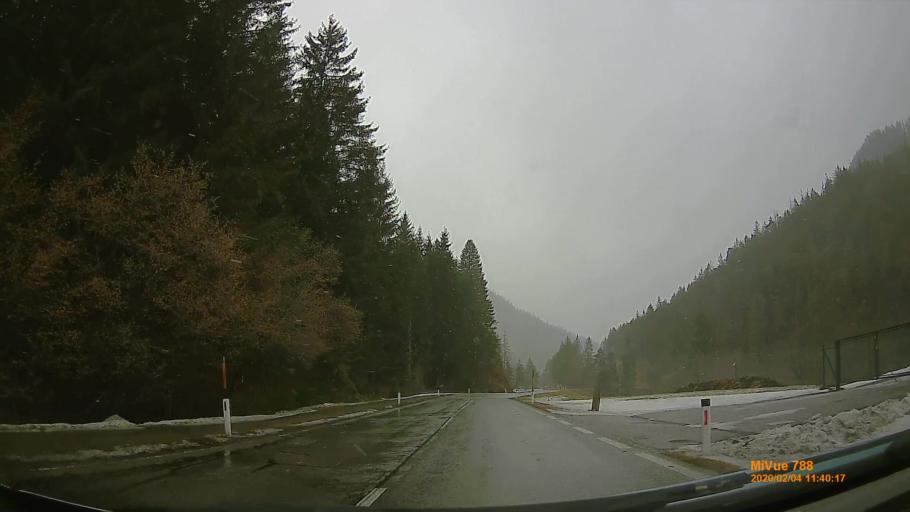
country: AT
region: Styria
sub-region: Politischer Bezirk Bruck-Muerzzuschlag
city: Muerzsteg
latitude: 47.6662
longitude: 15.5127
